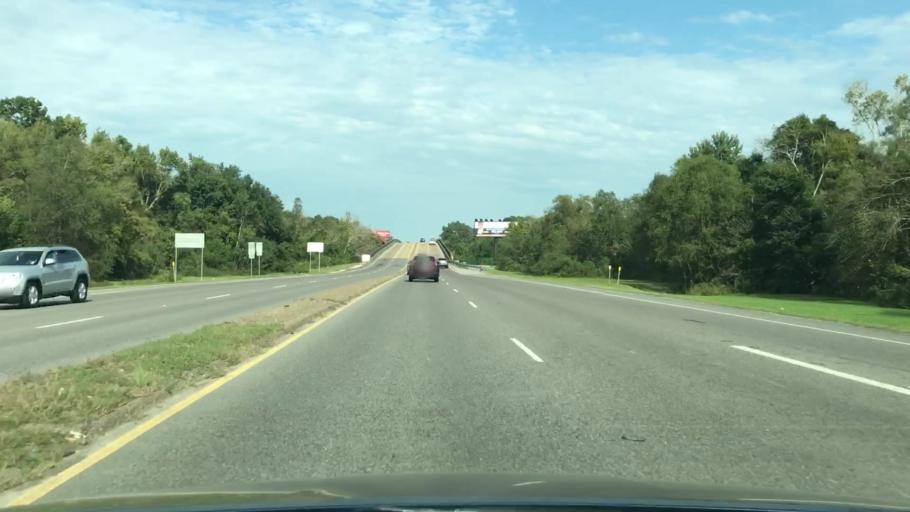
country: US
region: Louisiana
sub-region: Jefferson Parish
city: Bridge City
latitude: 29.9133
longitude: -90.1763
